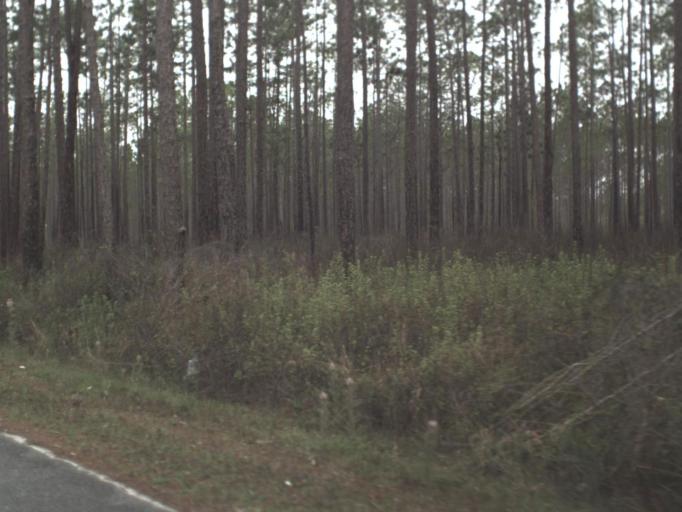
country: US
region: Florida
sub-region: Franklin County
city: Apalachicola
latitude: 29.9070
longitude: -84.9777
